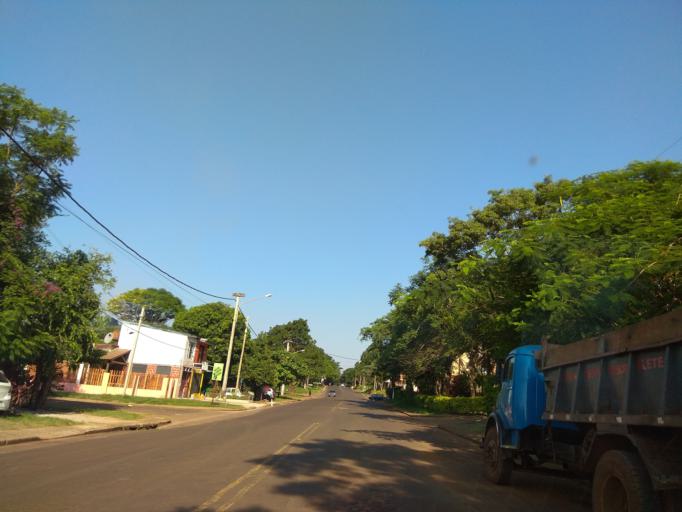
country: AR
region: Misiones
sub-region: Departamento de Capital
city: Posadas
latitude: -27.3646
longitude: -55.9251
